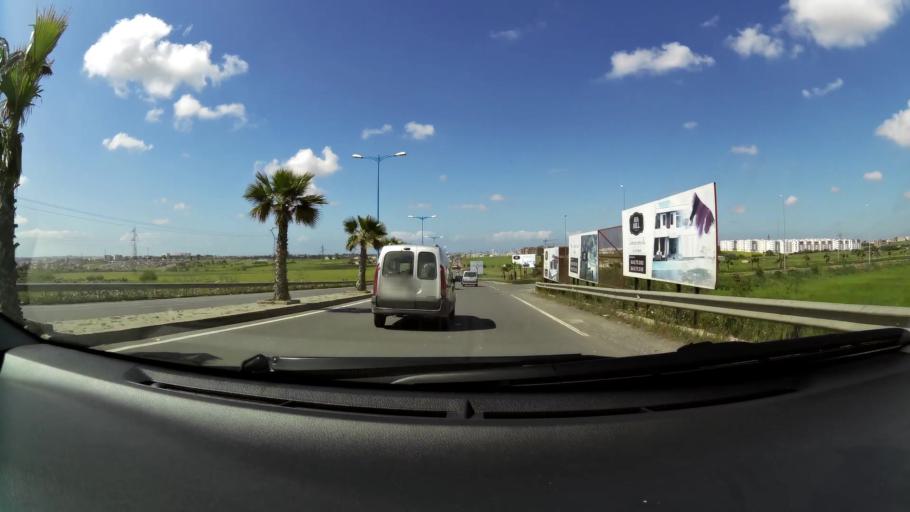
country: MA
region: Grand Casablanca
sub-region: Nouaceur
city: Bouskoura
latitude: 33.5127
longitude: -7.6132
